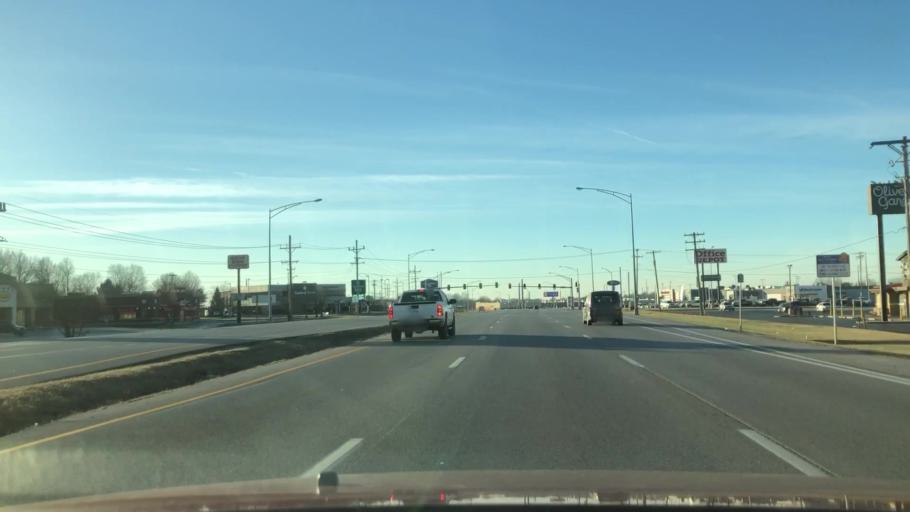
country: US
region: Missouri
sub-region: Greene County
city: Springfield
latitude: 37.1582
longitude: -93.2628
